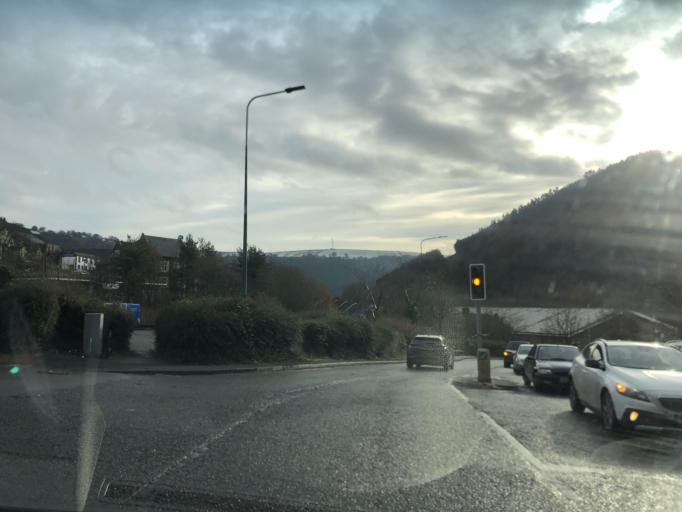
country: GB
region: Wales
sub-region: Blaenau Gwent
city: Abertillery
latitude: 51.7308
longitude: -3.1378
